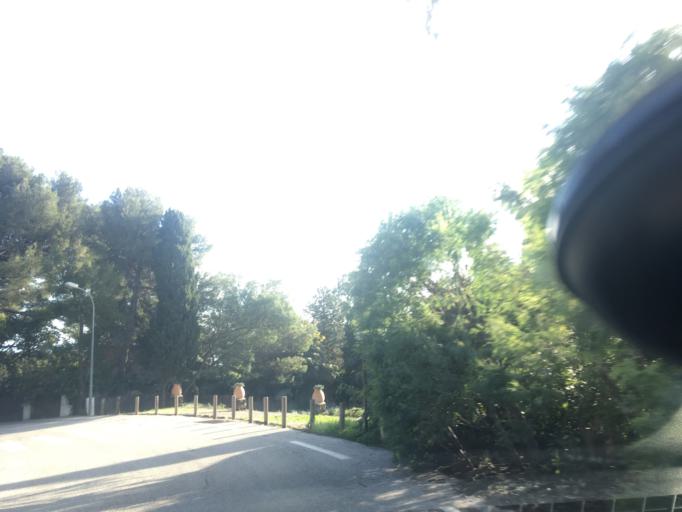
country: FR
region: Provence-Alpes-Cote d'Azur
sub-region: Departement du Var
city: Cavalaire-sur-Mer
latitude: 43.1575
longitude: 6.4775
